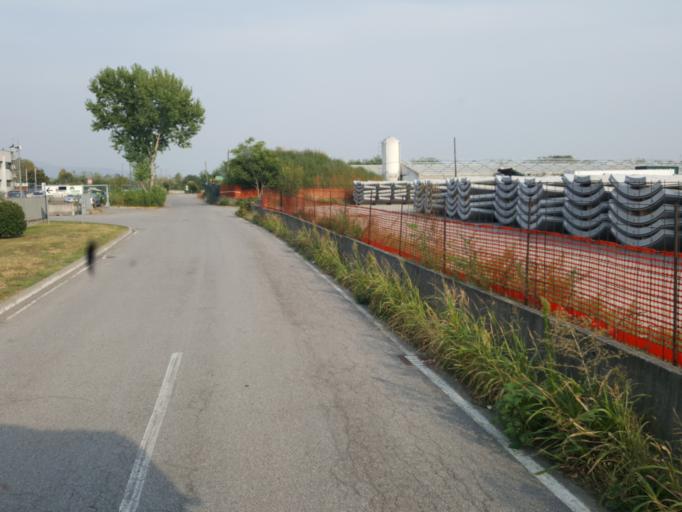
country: IT
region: Lombardy
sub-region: Provincia di Bergamo
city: Bolgare
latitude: 45.6162
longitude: 9.8149
